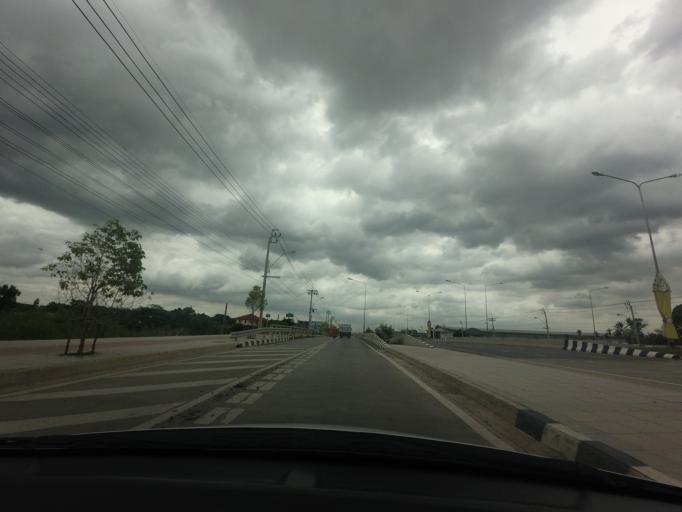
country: TH
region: Bangkok
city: Saphan Sung
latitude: 13.7539
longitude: 100.7092
